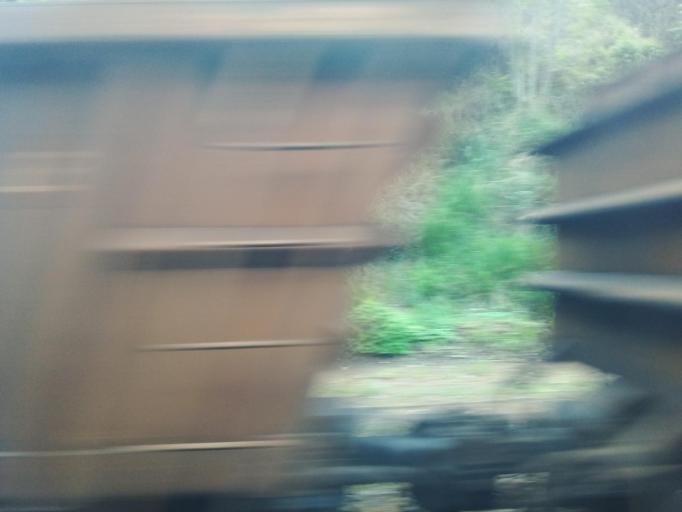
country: BR
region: Minas Gerais
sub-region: Rio Piracicaba
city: Rio Piracicaba
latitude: -19.9676
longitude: -43.2574
